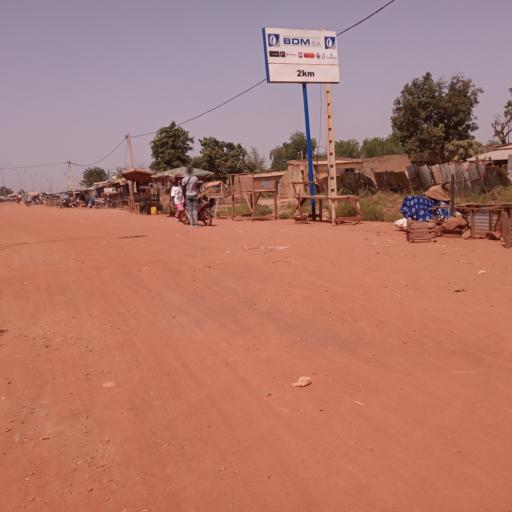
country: ML
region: Bamako
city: Bamako
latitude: 12.4759
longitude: -8.0556
